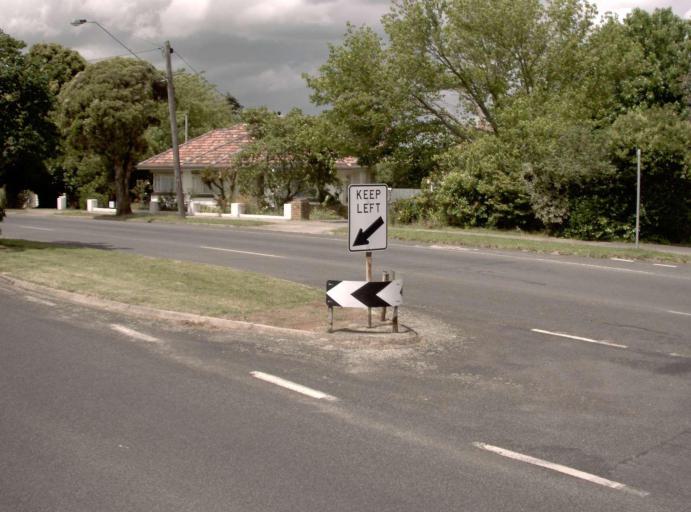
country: AU
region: Victoria
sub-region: Baw Baw
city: Warragul
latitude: -38.1545
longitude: 145.9338
